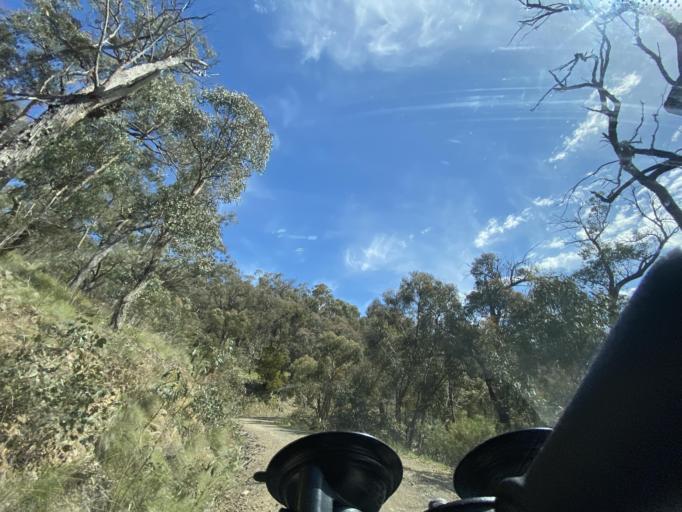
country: AU
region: Victoria
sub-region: Mansfield
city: Mansfield
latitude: -36.8073
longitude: 146.1072
